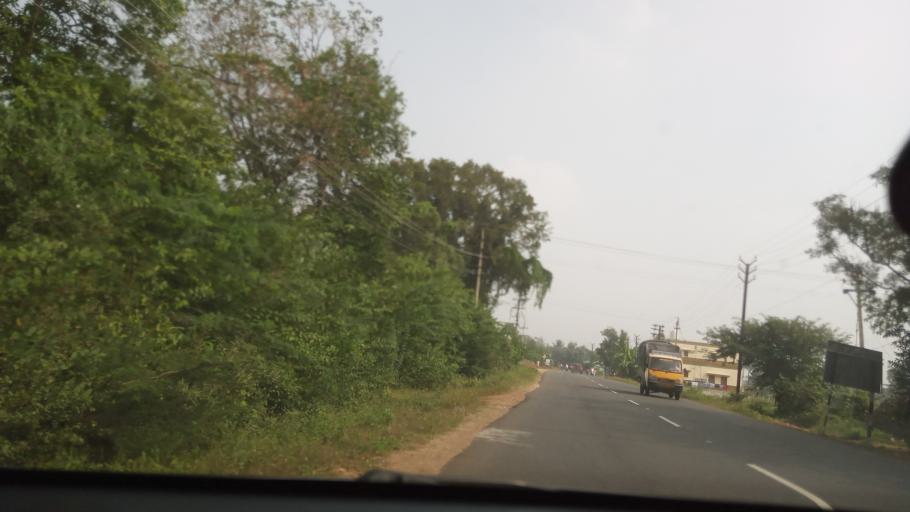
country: IN
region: Tamil Nadu
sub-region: Erode
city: Punjai Puliyampatti
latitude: 11.3317
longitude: 77.1535
